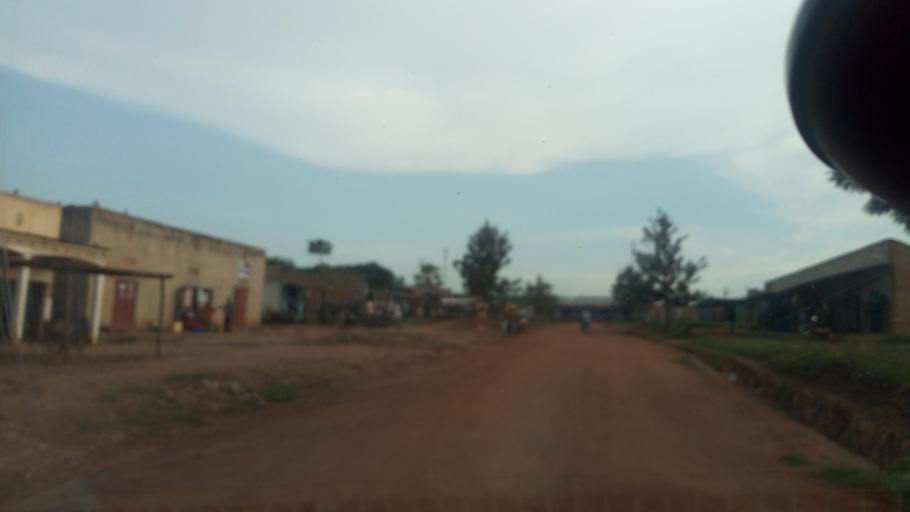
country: UG
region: Western Region
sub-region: Kiryandongo District
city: Kiryandongo
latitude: 1.8122
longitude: 32.0109
